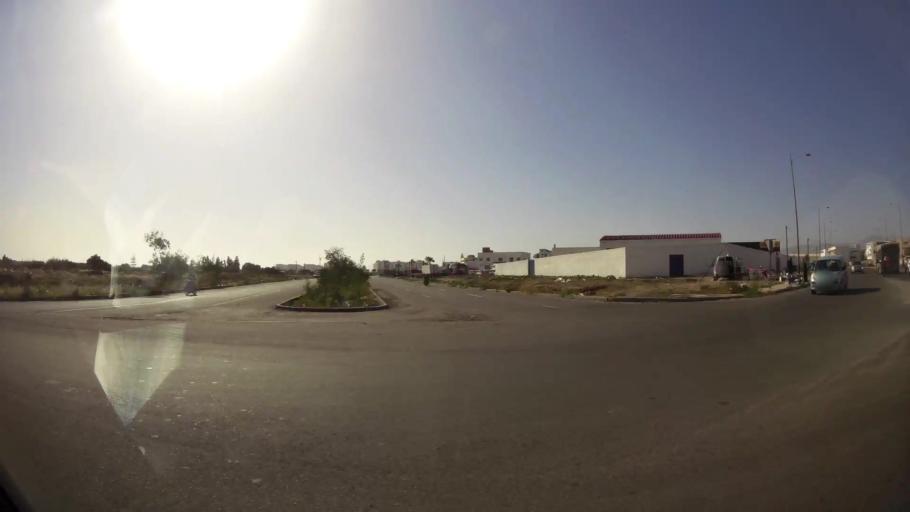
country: MA
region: Souss-Massa-Draa
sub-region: Inezgane-Ait Mellou
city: Inezgane
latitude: 30.3806
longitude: -9.5184
